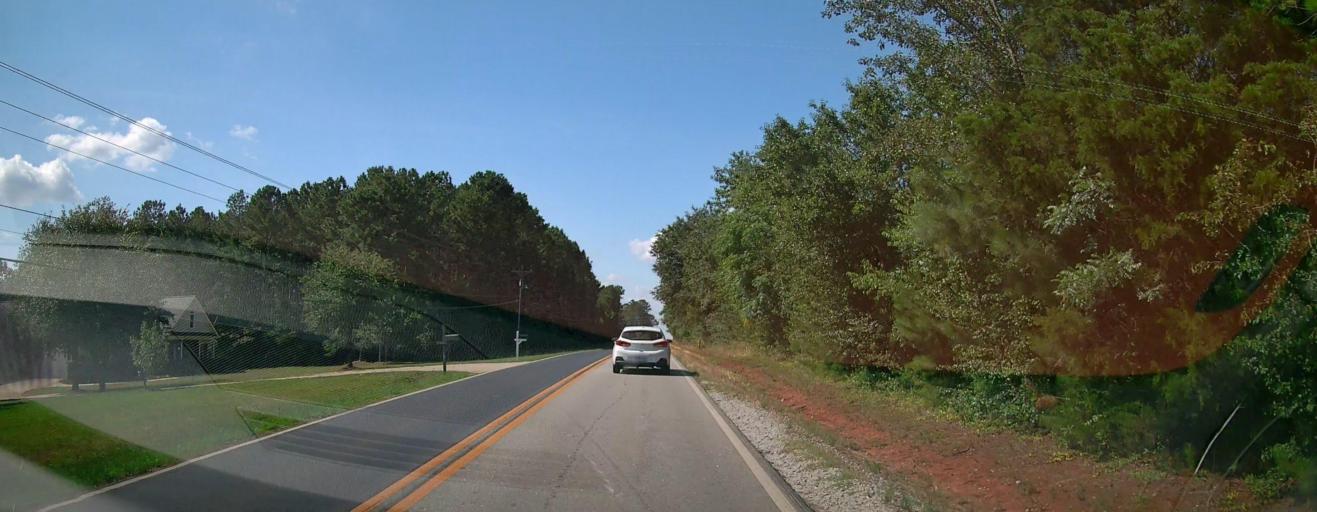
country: US
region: Georgia
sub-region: Spalding County
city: East Griffin
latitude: 33.2887
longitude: -84.1898
